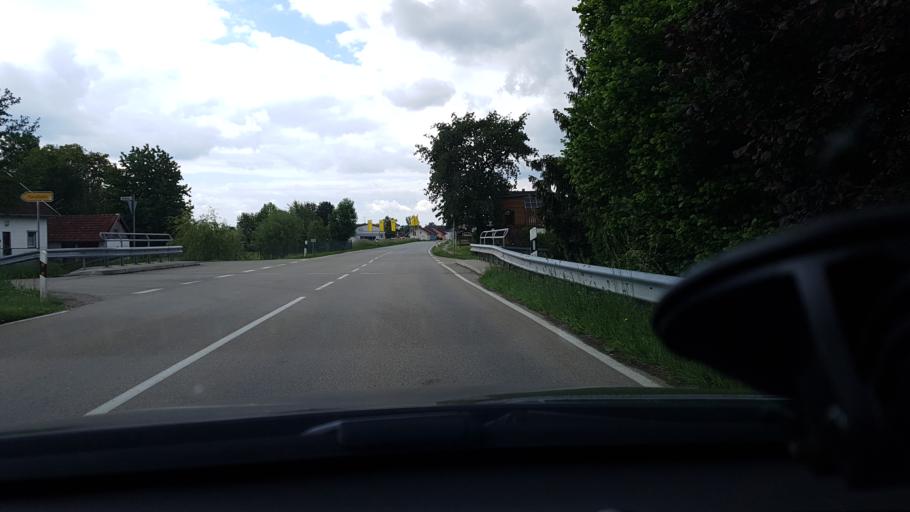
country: DE
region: Bavaria
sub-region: Lower Bavaria
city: Malching
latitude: 48.3179
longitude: 13.1959
